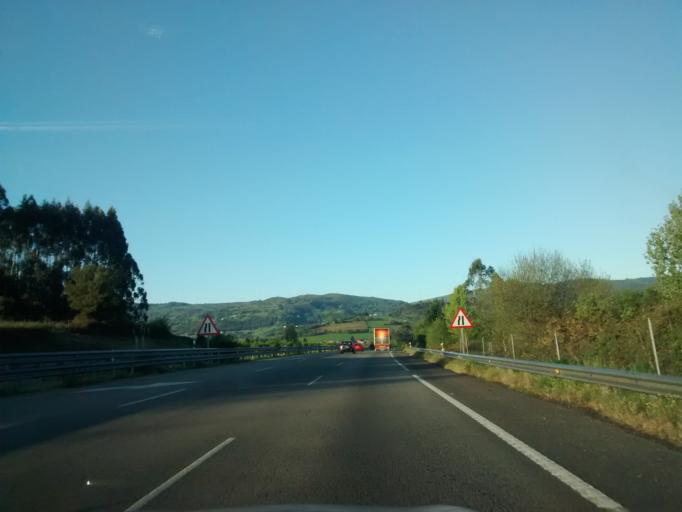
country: ES
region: Asturias
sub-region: Province of Asturias
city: Villaviciosa
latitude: 43.4778
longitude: -5.4608
